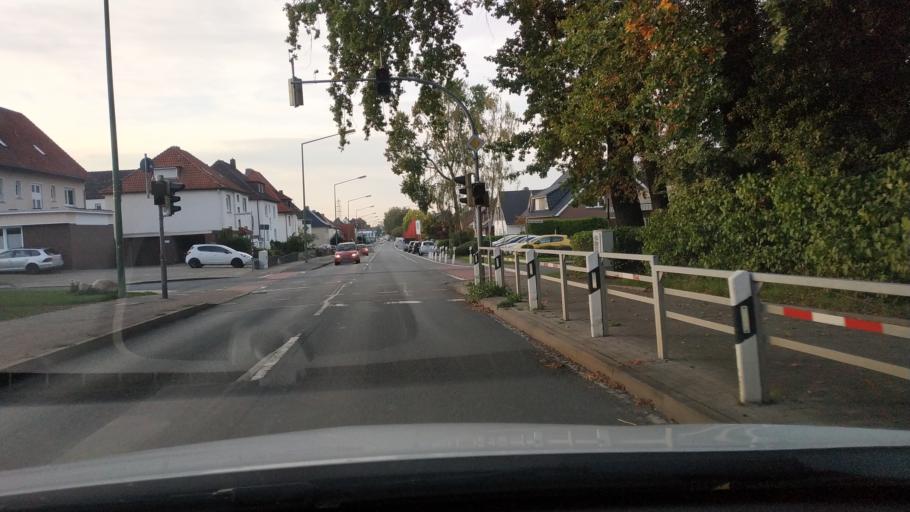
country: DE
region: Lower Saxony
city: Belm
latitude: 52.2505
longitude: 8.1043
